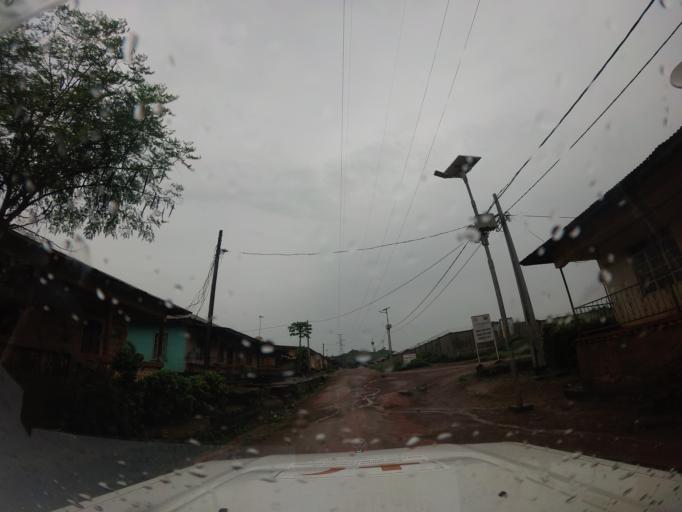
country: SL
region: Northern Province
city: Makeni
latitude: 8.8830
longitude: -12.0500
